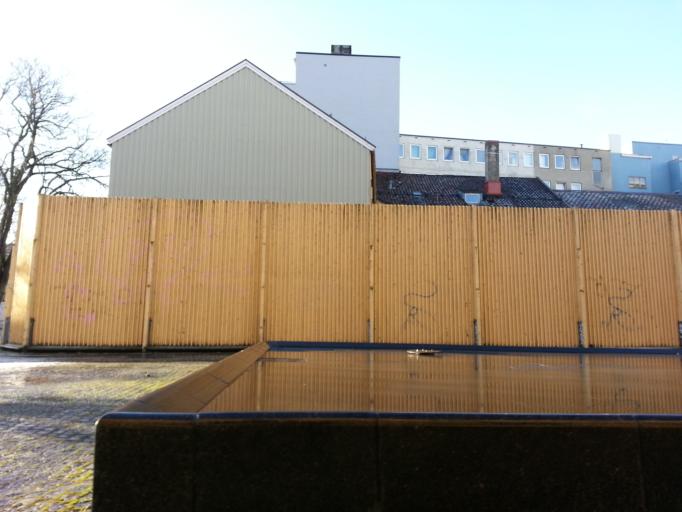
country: NO
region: Sor-Trondelag
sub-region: Trondheim
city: Trondheim
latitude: 63.4325
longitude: 10.4028
